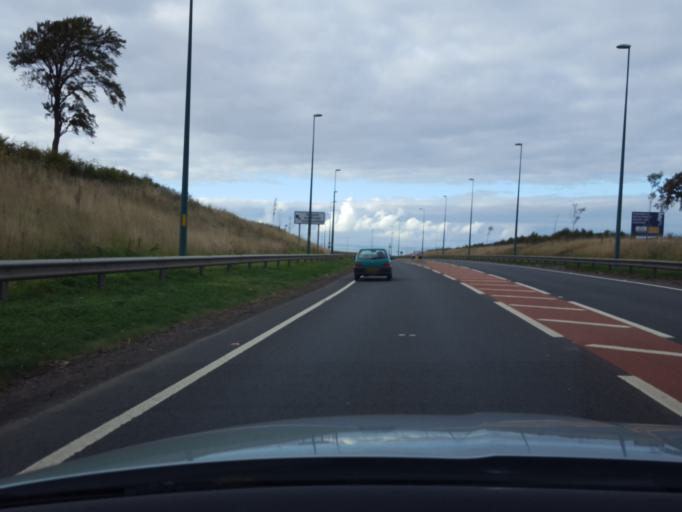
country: GB
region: Scotland
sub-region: Fife
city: Pathhead
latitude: 55.8912
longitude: -2.9974
